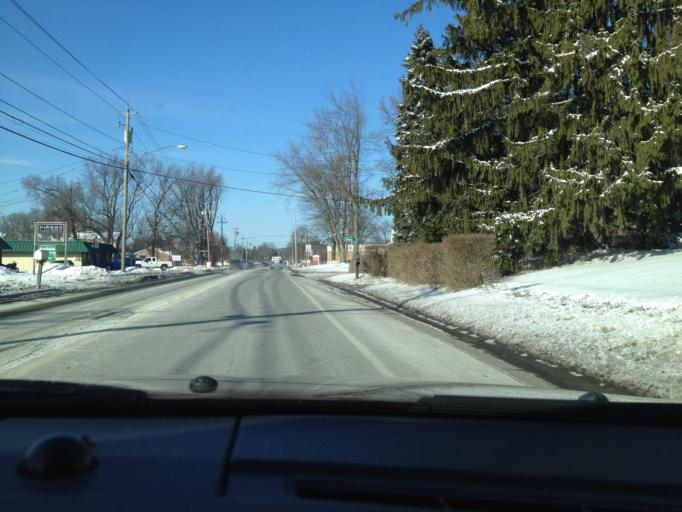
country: US
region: New York
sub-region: Albany County
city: West Albany
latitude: 42.7032
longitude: -73.7752
